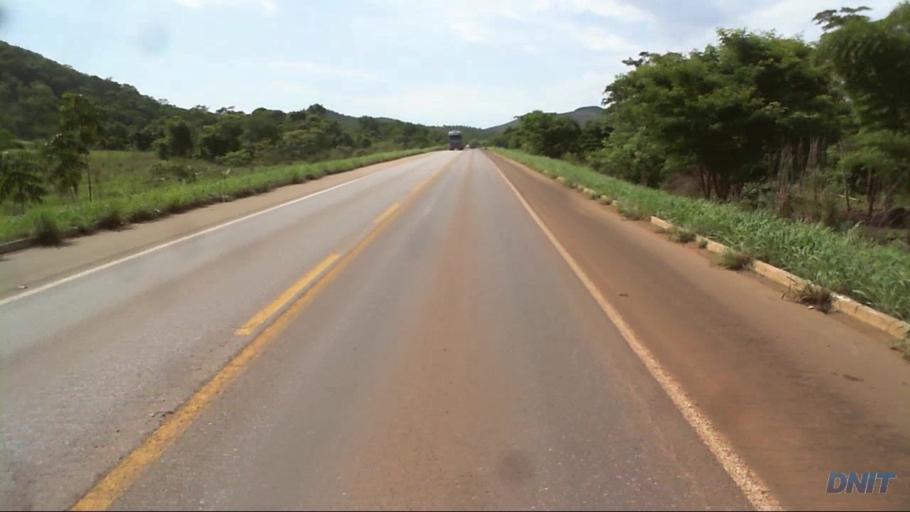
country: BR
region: Goias
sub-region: Barro Alto
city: Barro Alto
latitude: -15.1246
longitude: -48.8363
